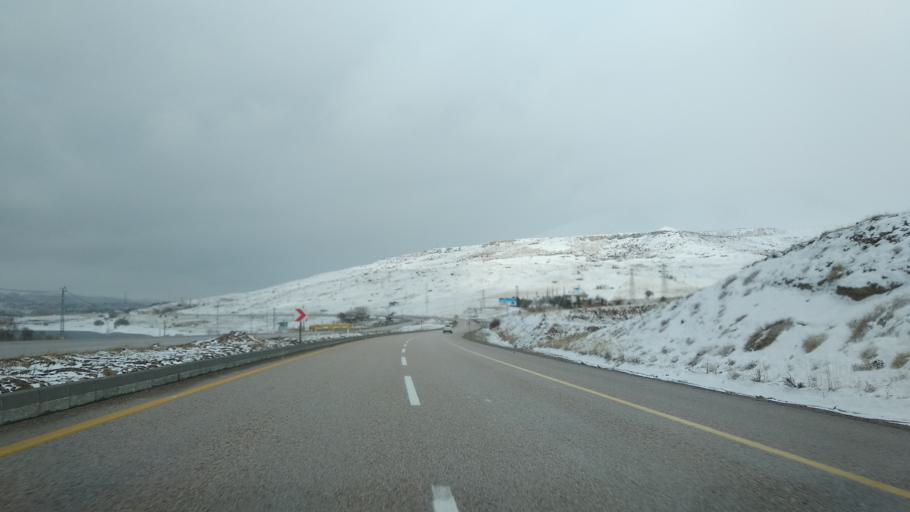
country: TR
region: Kayseri
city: Pinarbasi
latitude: 38.6992
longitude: 36.3660
